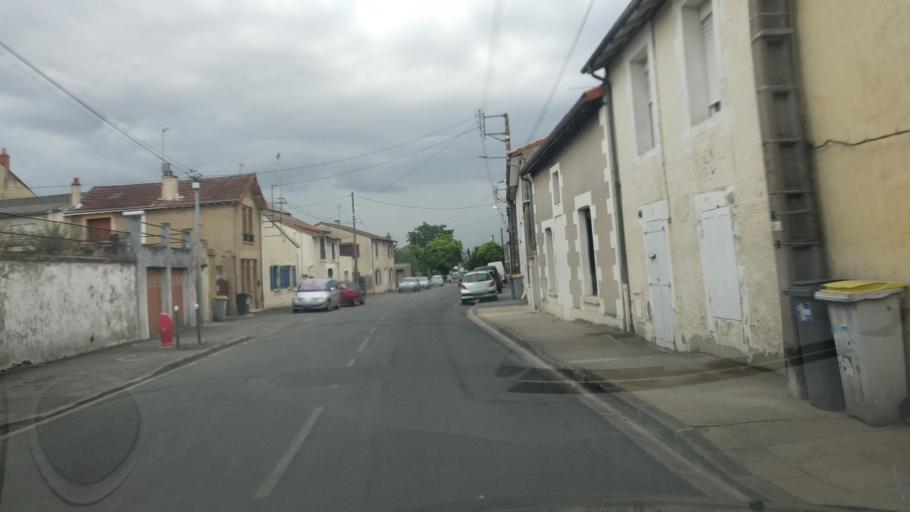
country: FR
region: Poitou-Charentes
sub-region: Departement de la Vienne
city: Poitiers
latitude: 46.5945
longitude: 0.3334
